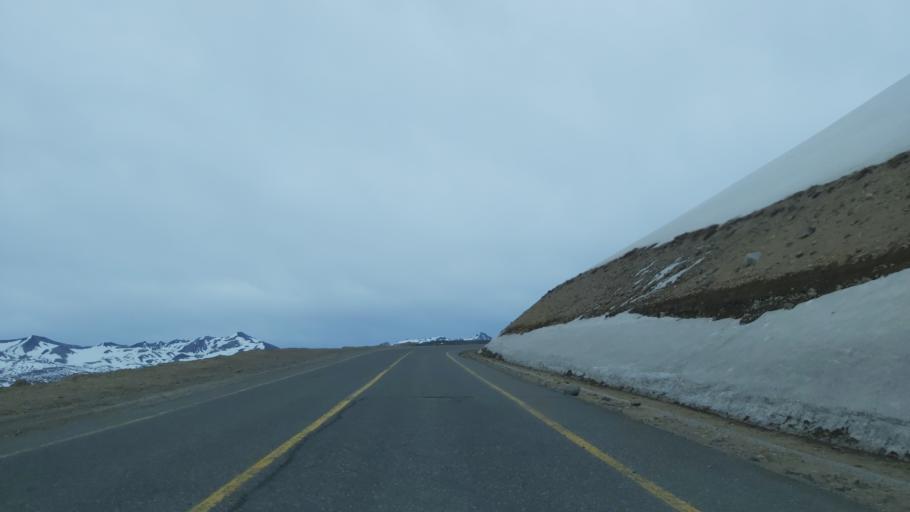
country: CL
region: Maule
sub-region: Provincia de Linares
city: Colbun
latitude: -36.0223
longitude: -70.5013
